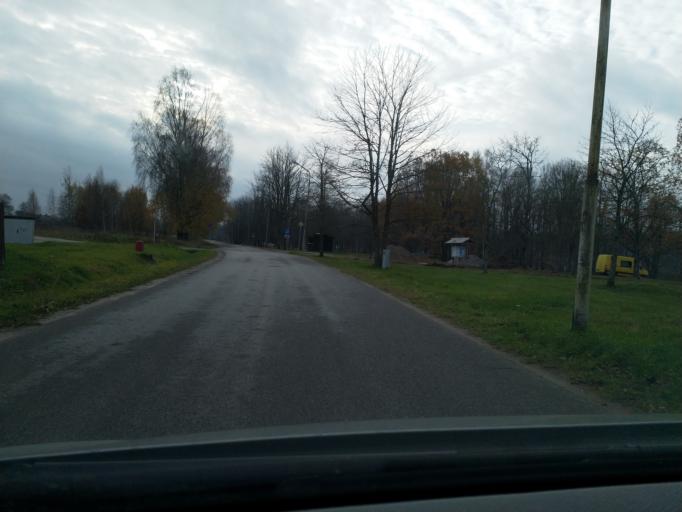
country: LV
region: Kuldigas Rajons
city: Kuldiga
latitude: 56.9732
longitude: 21.9780
